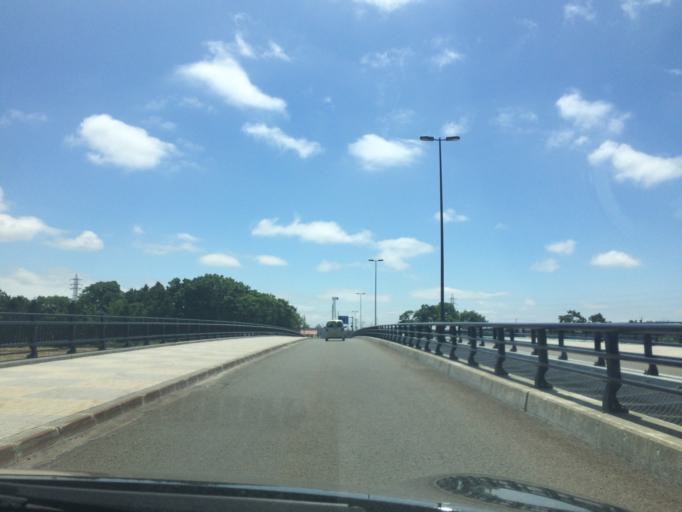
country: JP
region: Hokkaido
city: Tobetsu
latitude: 43.2142
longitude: 141.5172
